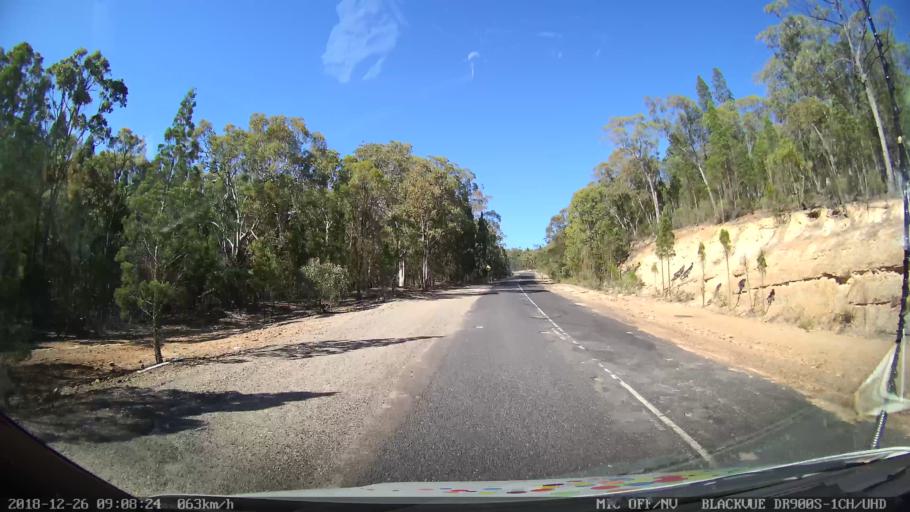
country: AU
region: New South Wales
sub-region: Mid-Western Regional
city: Kandos
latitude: -32.7159
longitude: 150.0025
